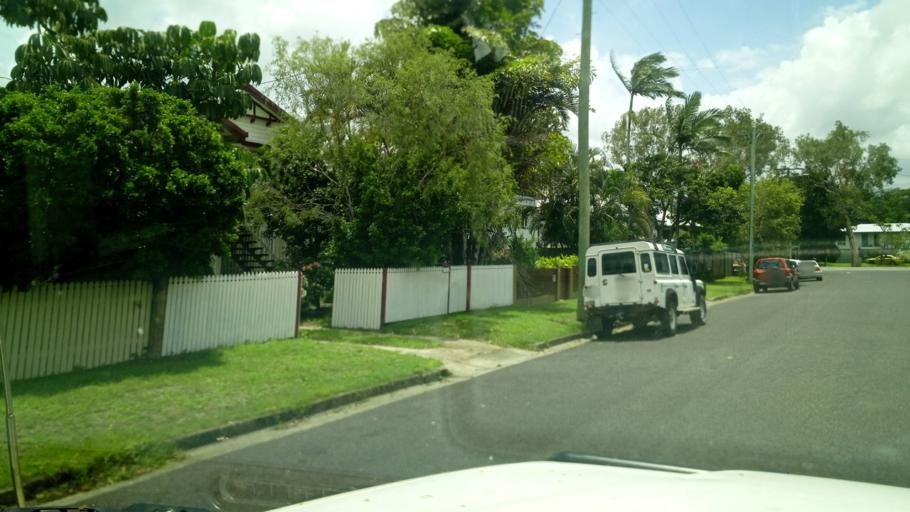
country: AU
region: Queensland
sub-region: Cairns
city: Cairns
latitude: -16.9145
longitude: 145.7572
